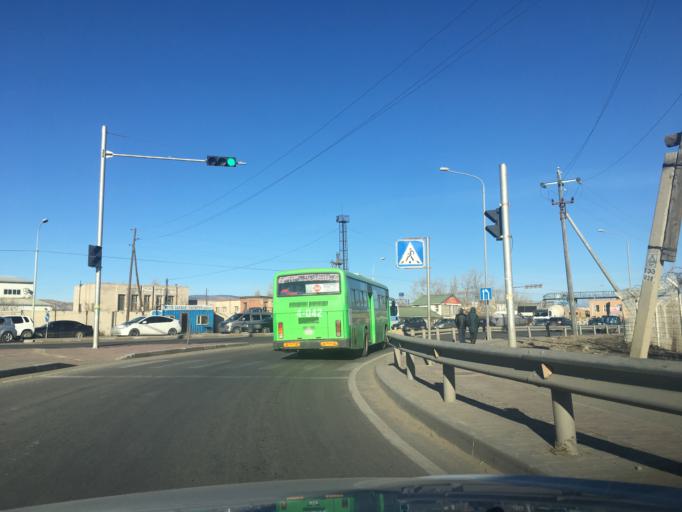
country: MN
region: Ulaanbaatar
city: Ulaanbaatar
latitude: 47.9070
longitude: 106.7862
